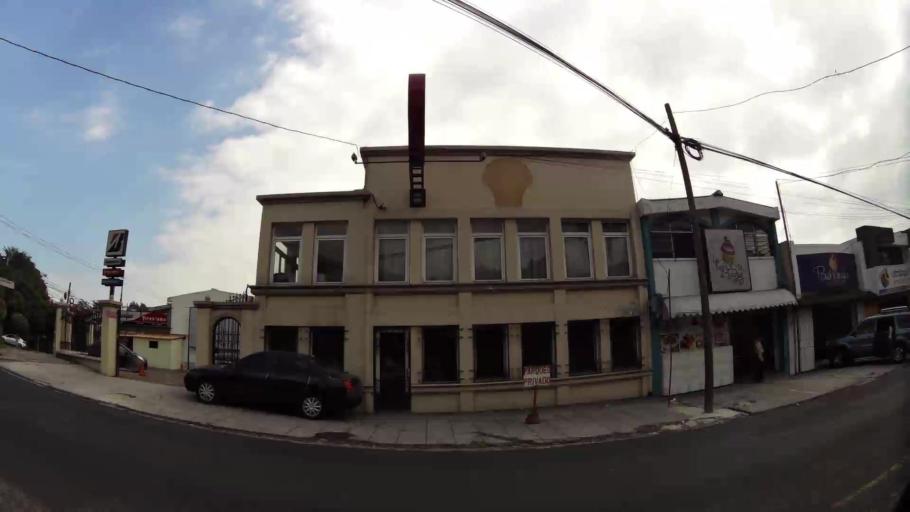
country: SV
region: San Salvador
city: Mejicanos
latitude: 13.7114
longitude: -89.2479
